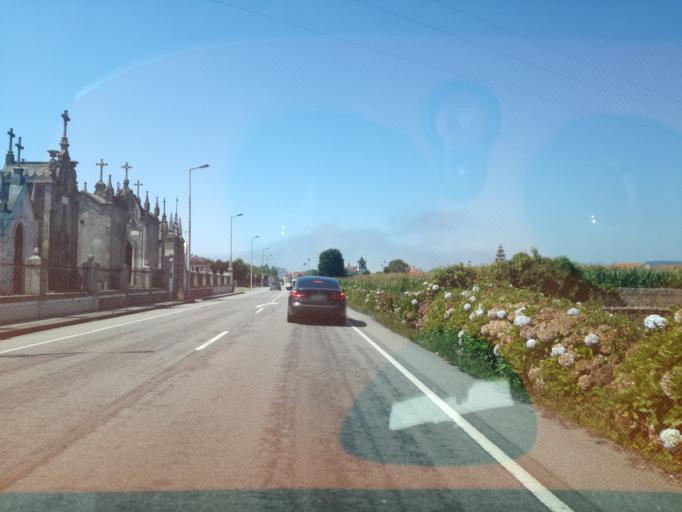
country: PT
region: Braga
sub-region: Esposende
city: Apulia
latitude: 41.5071
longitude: -8.7651
